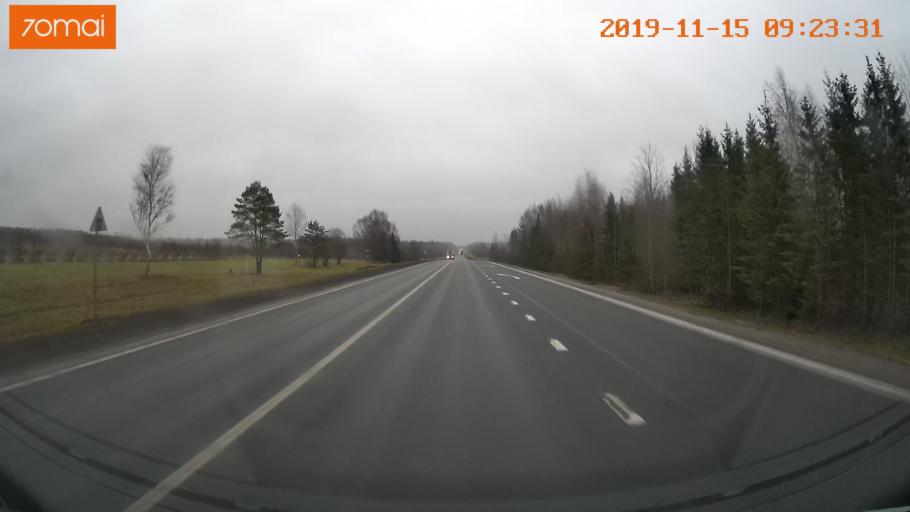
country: RU
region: Vologda
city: Tonshalovo
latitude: 59.3010
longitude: 38.1135
